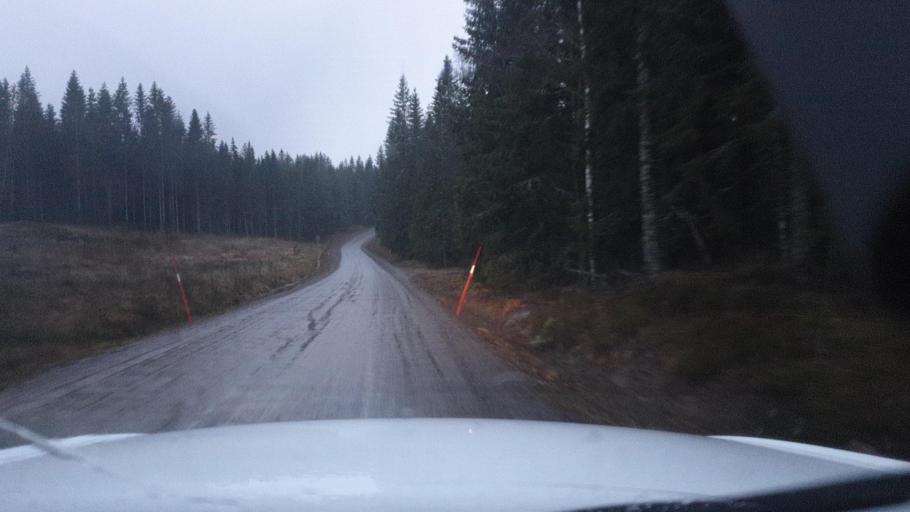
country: SE
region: Vaermland
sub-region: Sunne Kommun
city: Sunne
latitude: 59.8381
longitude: 12.9267
